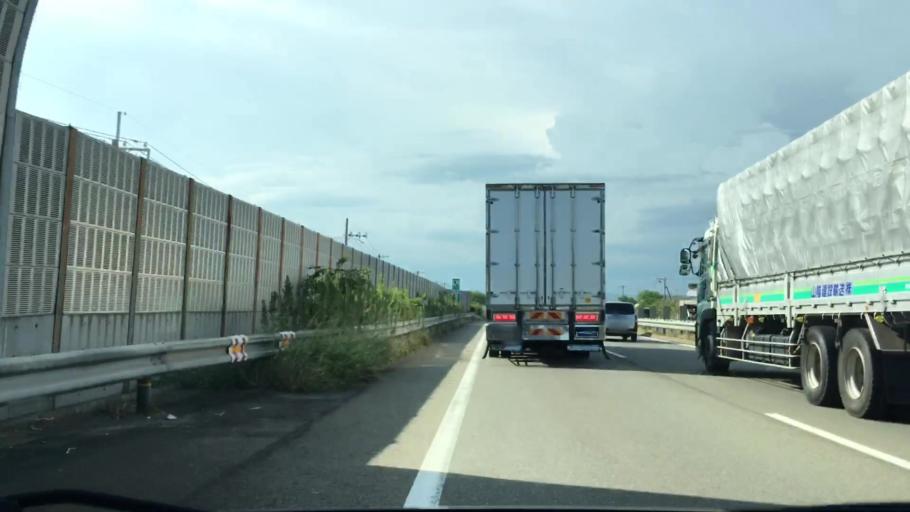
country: JP
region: Hyogo
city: Kakogawacho-honmachi
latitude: 34.7258
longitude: 134.8928
